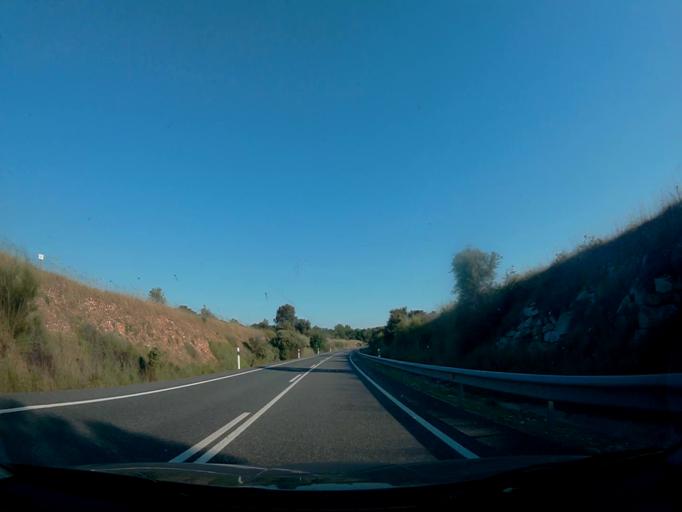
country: ES
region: Castille-La Mancha
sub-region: Province of Toledo
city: Escalona
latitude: 40.1816
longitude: -4.3998
